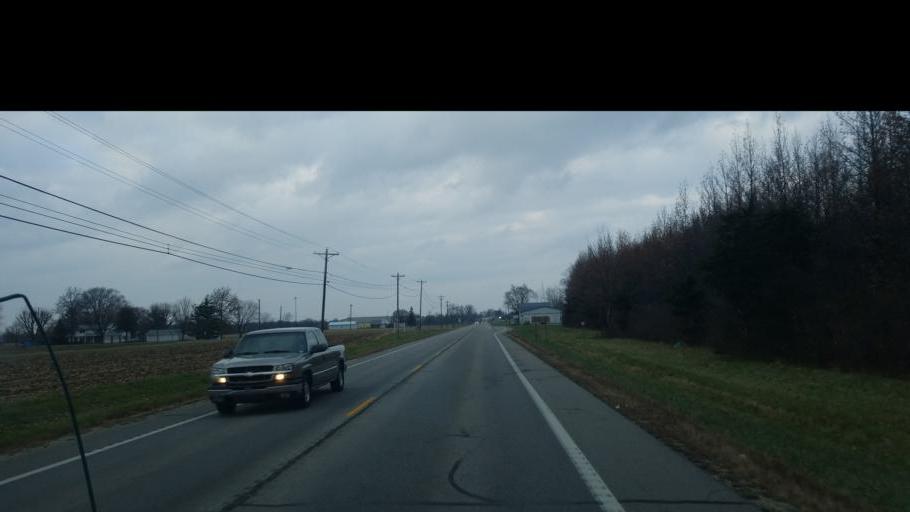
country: US
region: Ohio
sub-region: Mercer County
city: Celina
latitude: 40.5254
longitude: -84.5772
